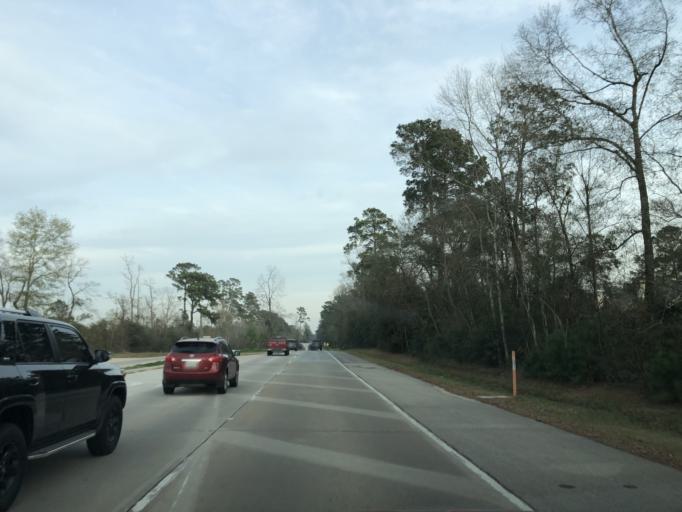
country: US
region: Texas
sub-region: Montgomery County
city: The Woodlands
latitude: 30.2156
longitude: -95.5617
